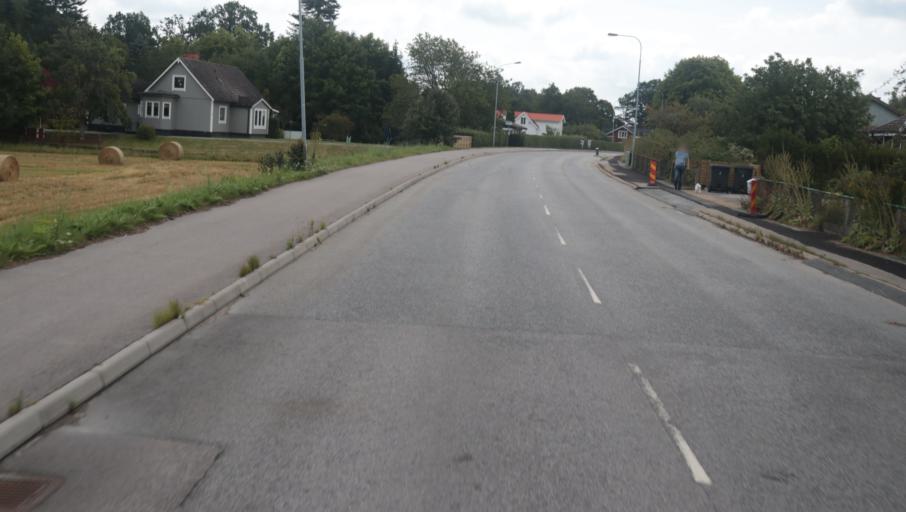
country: SE
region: Blekinge
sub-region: Karlshamns Kommun
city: Karlshamn
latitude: 56.2165
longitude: 14.8332
